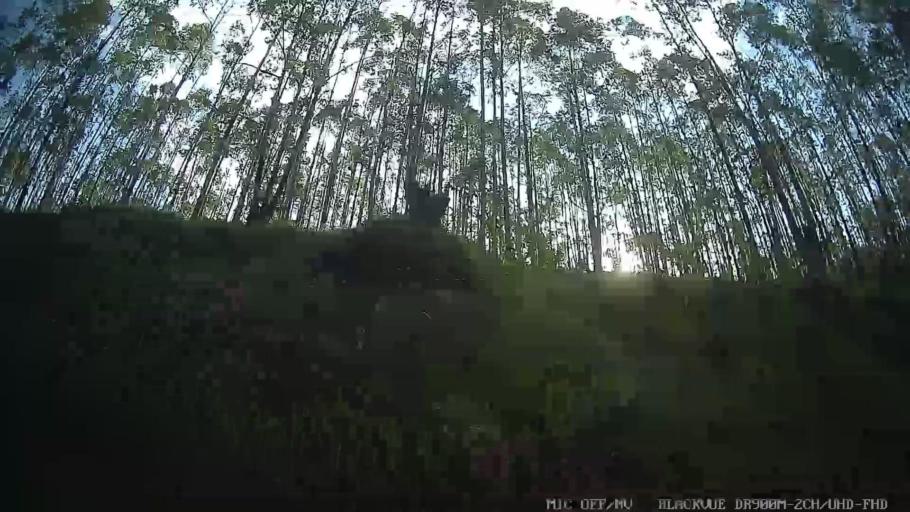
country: BR
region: Sao Paulo
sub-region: Serra Negra
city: Serra Negra
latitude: -22.6576
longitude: -46.6891
